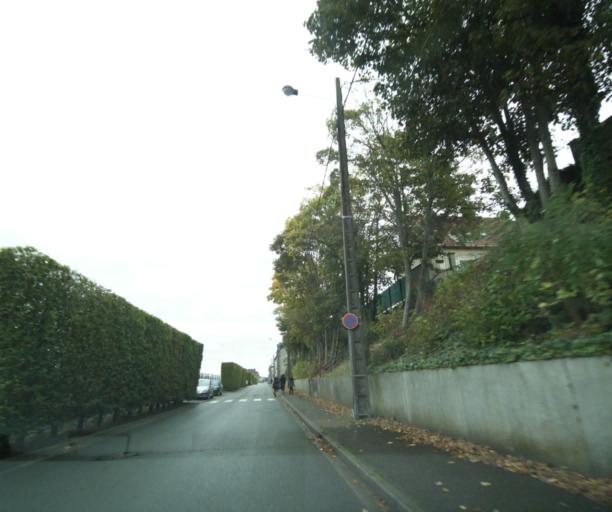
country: FR
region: Centre
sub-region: Departement d'Eure-et-Loir
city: Dreux
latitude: 48.7305
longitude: 1.3706
